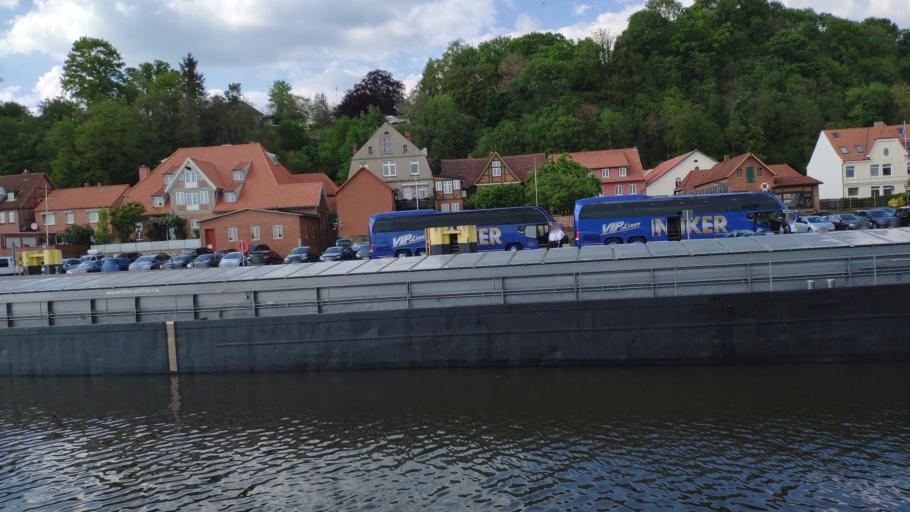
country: DE
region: Schleswig-Holstein
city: Lauenburg
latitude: 53.3698
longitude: 10.5595
